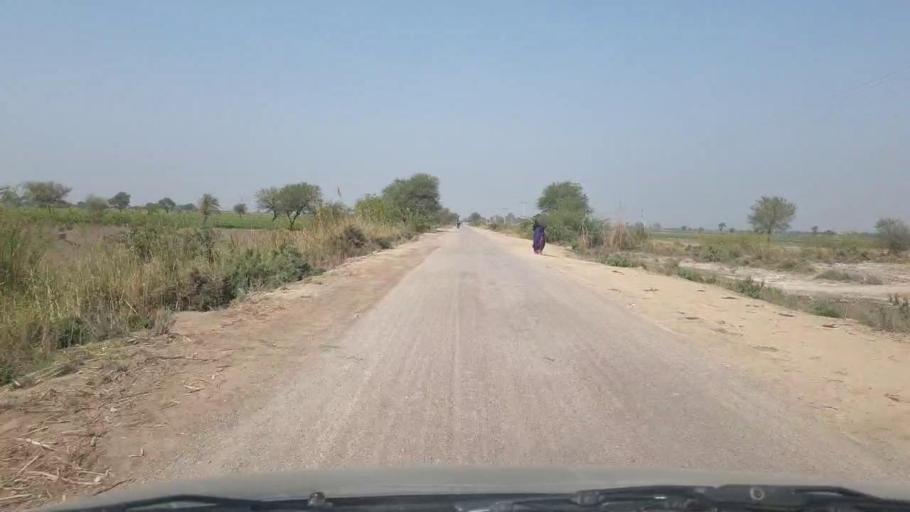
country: PK
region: Sindh
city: Mirwah Gorchani
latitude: 25.3222
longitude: 69.1515
